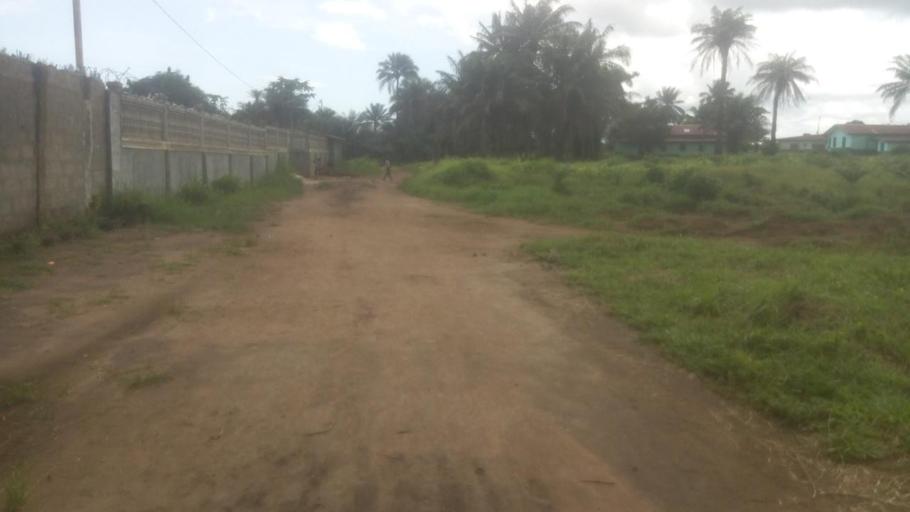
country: SL
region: Northern Province
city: Masoyila
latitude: 8.5864
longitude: -13.1683
